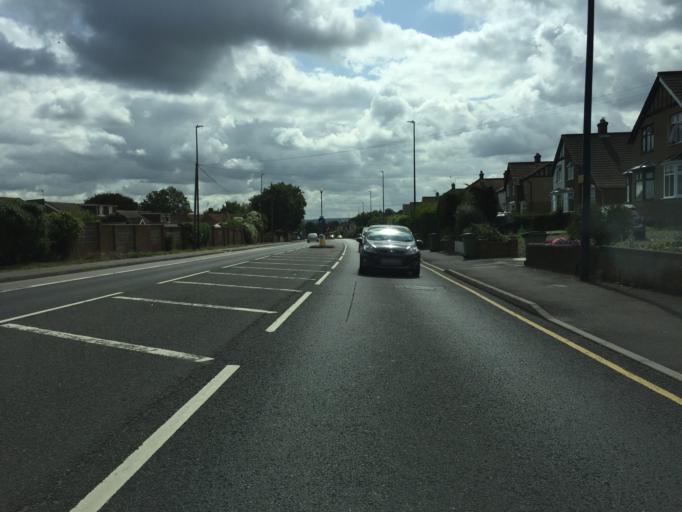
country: GB
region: England
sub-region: Kent
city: Maidstone
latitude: 51.2835
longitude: 0.4989
